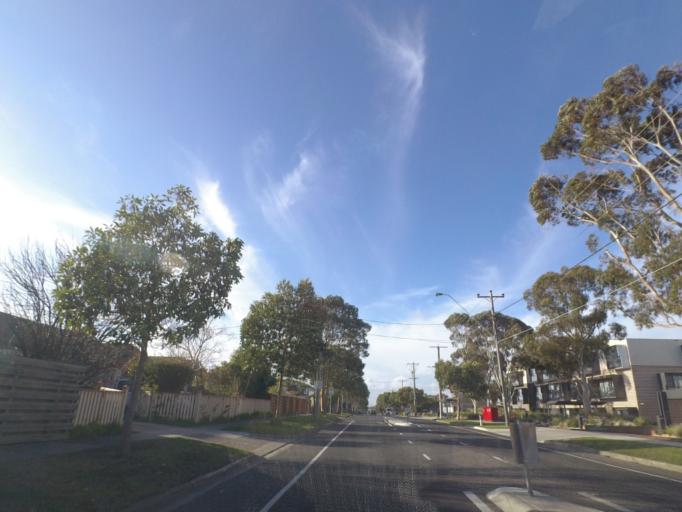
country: AU
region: Victoria
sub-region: Whitehorse
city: Box Hill
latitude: -37.8169
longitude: 145.1310
